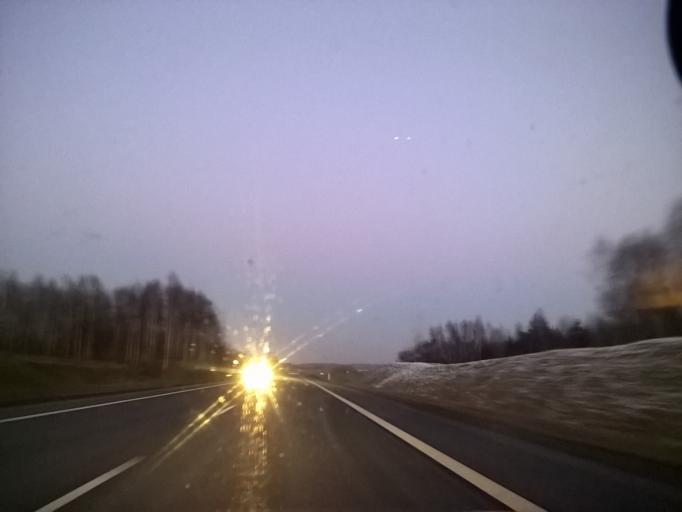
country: PL
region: Warmian-Masurian Voivodeship
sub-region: Powiat olsztynski
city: Biskupiec
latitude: 53.8318
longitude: 20.8994
